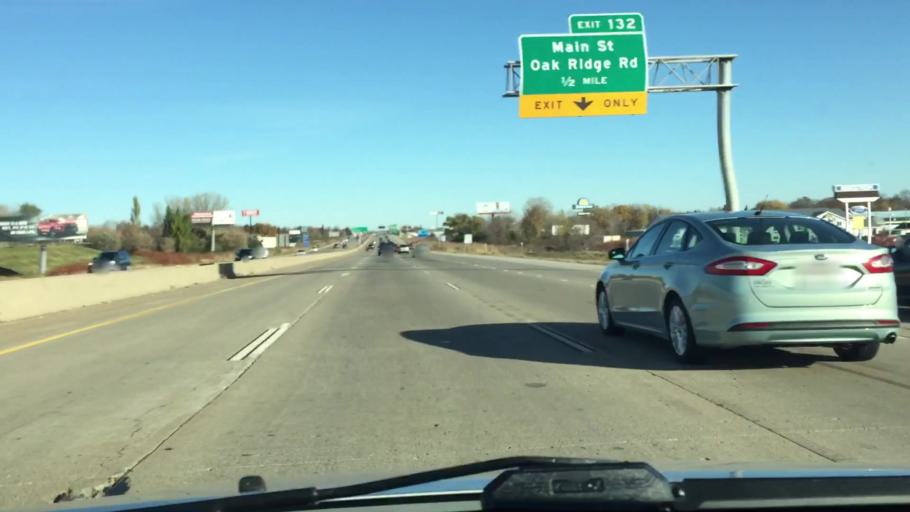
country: US
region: Wisconsin
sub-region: Winnebago County
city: Neenah
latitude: 44.1795
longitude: -88.4887
